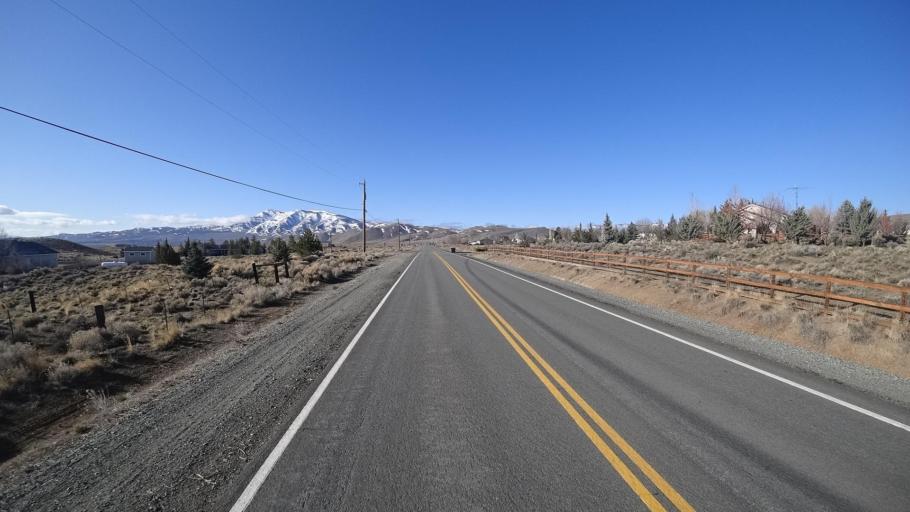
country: US
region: Nevada
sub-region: Washoe County
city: Cold Springs
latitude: 39.6874
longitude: -119.9181
